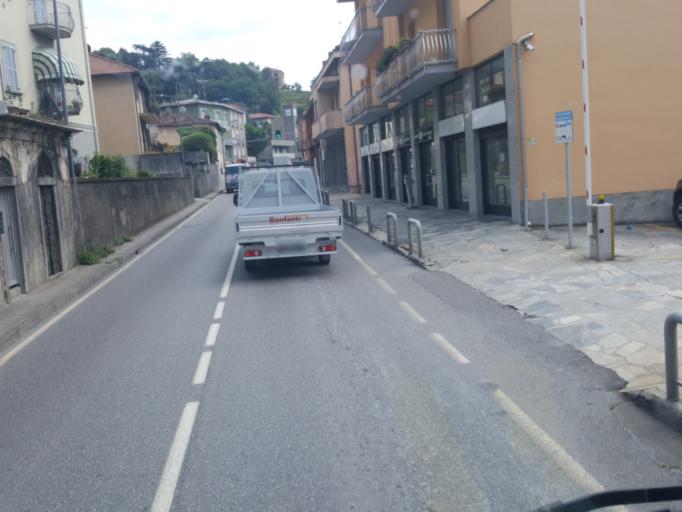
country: IT
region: Lombardy
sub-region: Provincia di Lecco
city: Vercurago
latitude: 45.8135
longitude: 9.4236
